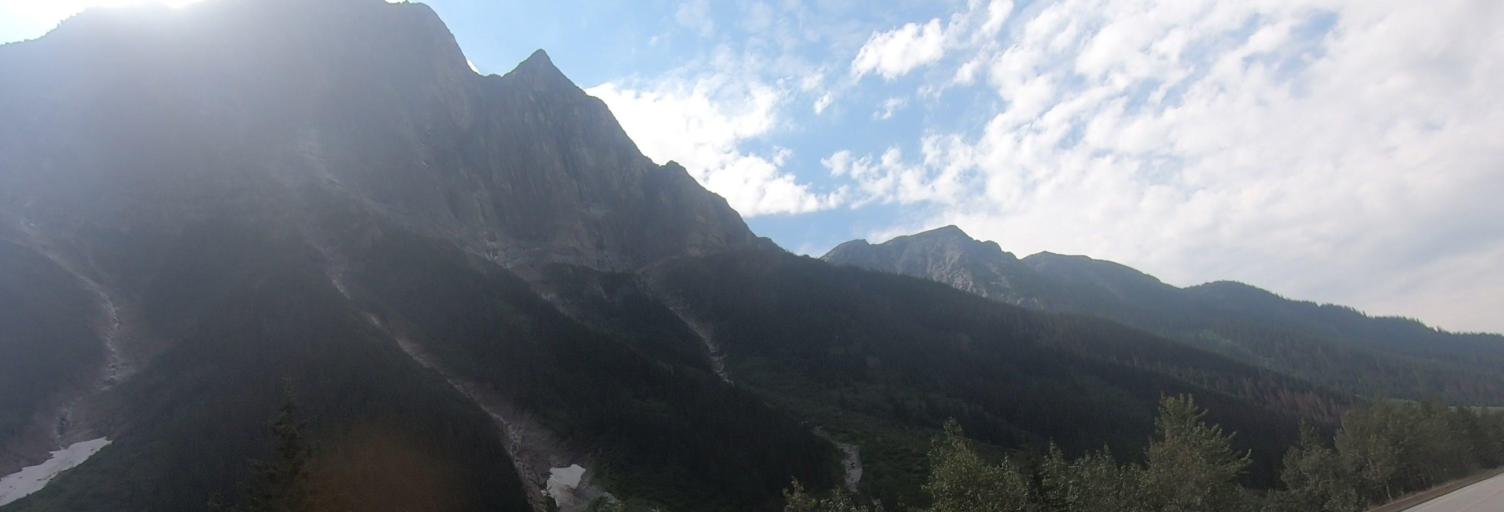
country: CA
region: British Columbia
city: Golden
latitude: 51.3259
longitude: -117.4750
